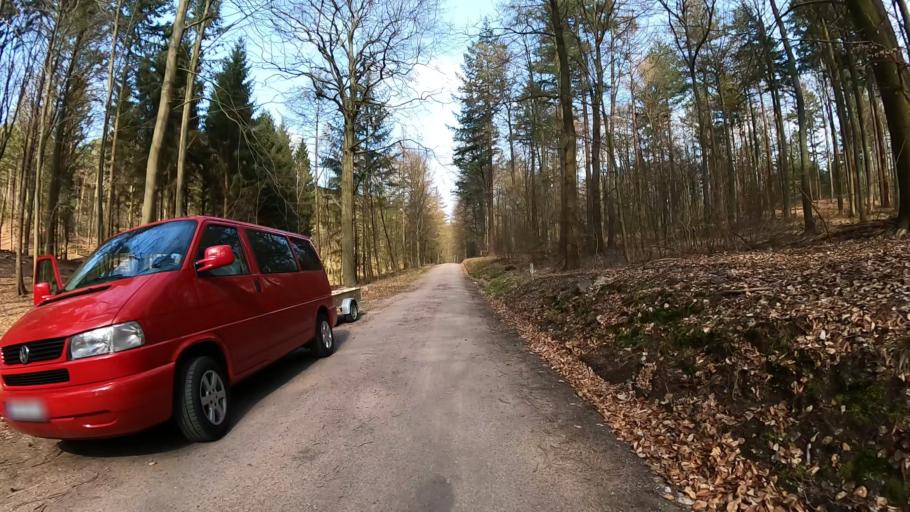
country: DE
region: Hamburg
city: Harburg
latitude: 53.4629
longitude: 9.9148
